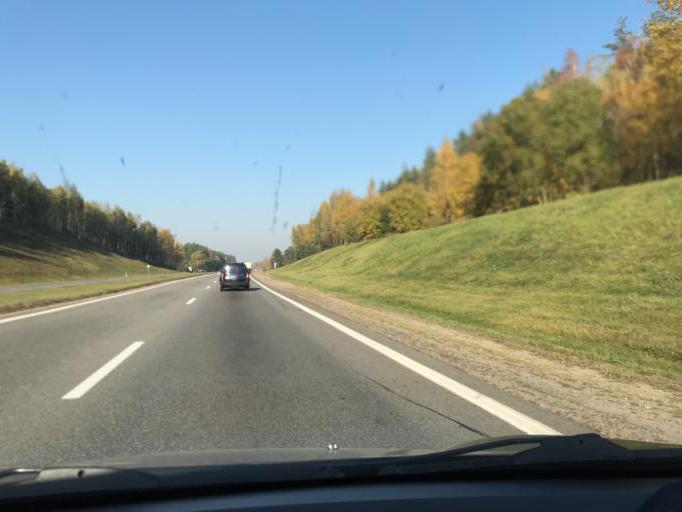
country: BY
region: Minsk
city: Luhavaya Slabada
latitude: 53.7655
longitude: 27.8278
